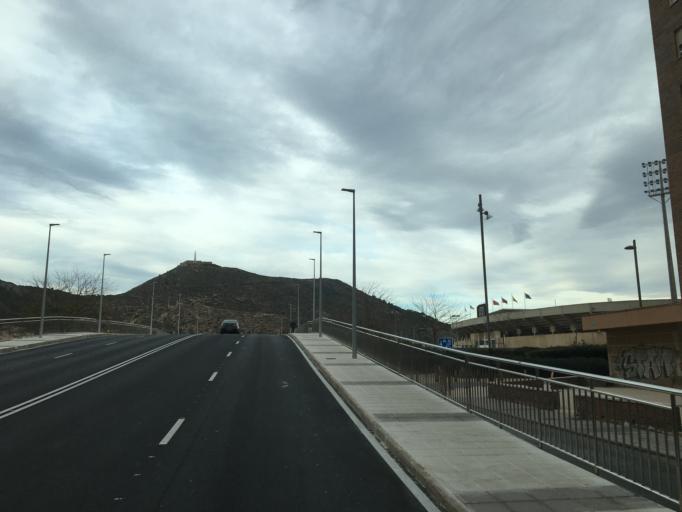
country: ES
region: Murcia
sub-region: Murcia
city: Cartagena
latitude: 37.6090
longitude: -0.9940
